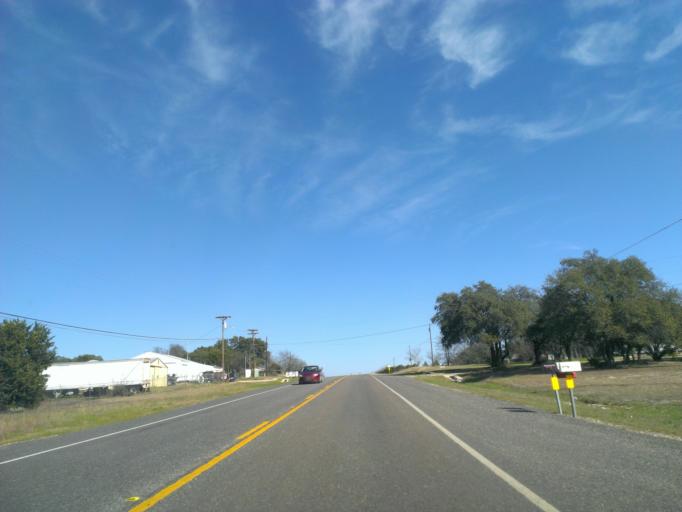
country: US
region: Texas
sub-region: Bell County
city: Belton
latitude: 31.0412
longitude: -97.5193
